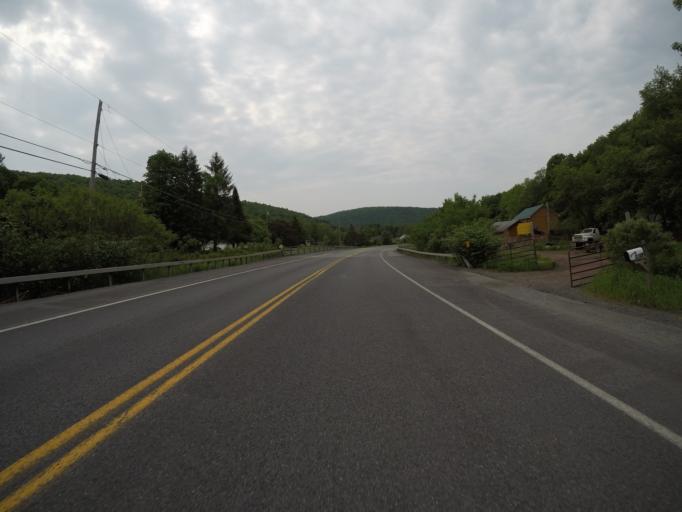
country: US
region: New York
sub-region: Sullivan County
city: Livingston Manor
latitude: 41.9793
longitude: -74.8936
